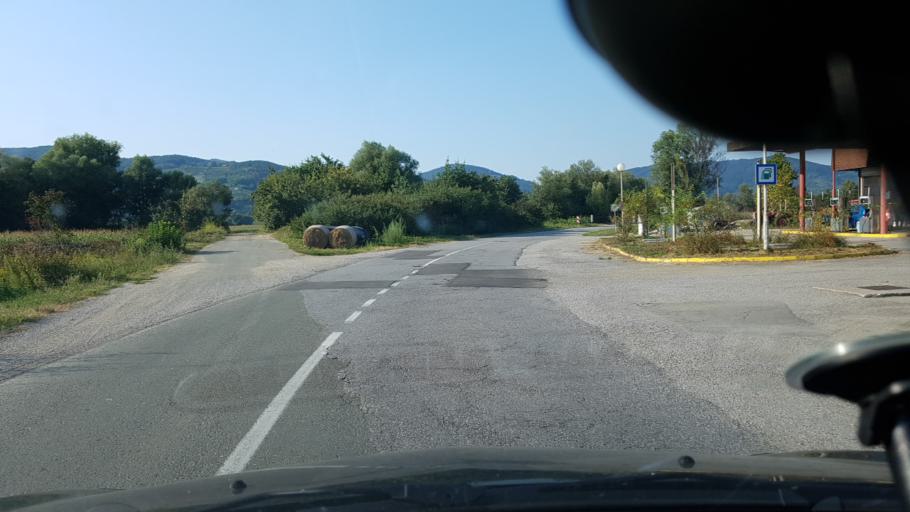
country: SI
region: Bistrica ob Sotli
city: Bistrica ob Sotli
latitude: 46.0109
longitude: 15.7157
